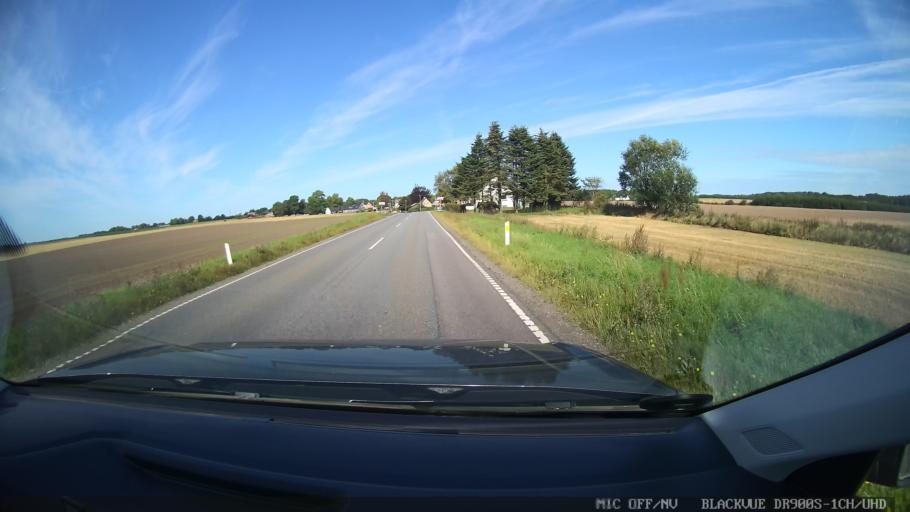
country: DK
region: North Denmark
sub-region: Mariagerfjord Kommune
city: Mariager
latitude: 56.6905
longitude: 9.9837
